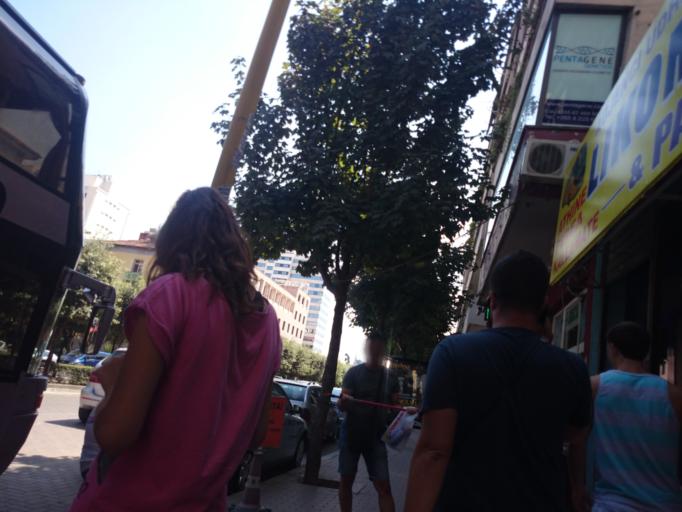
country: AL
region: Tirane
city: Tirana
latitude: 41.3315
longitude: 19.8174
